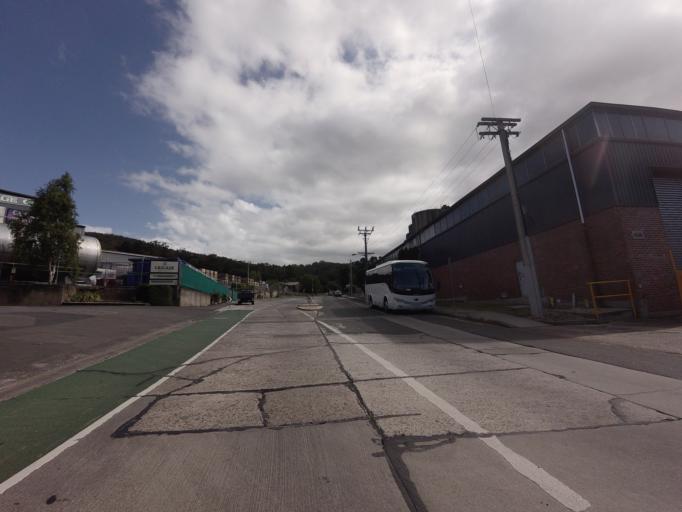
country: AU
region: Tasmania
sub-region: Hobart
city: Dynnyrne
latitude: -42.8963
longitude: 147.2926
